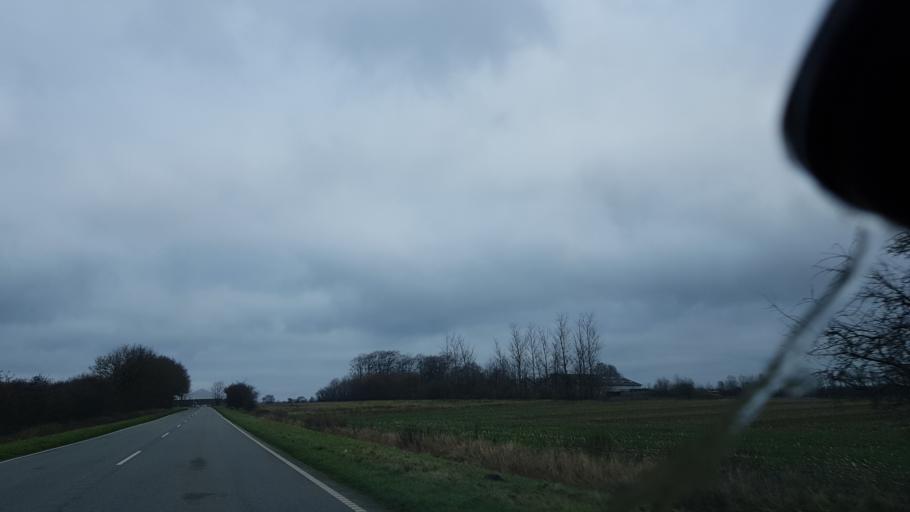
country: DK
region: South Denmark
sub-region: Haderslev Kommune
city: Vojens
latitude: 55.2386
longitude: 9.2175
